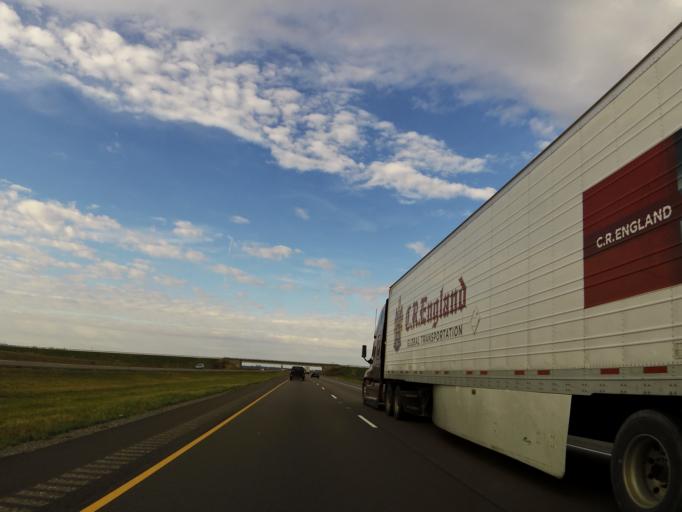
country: US
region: Illinois
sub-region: Washington County
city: Okawville
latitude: 38.4277
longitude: -89.4738
